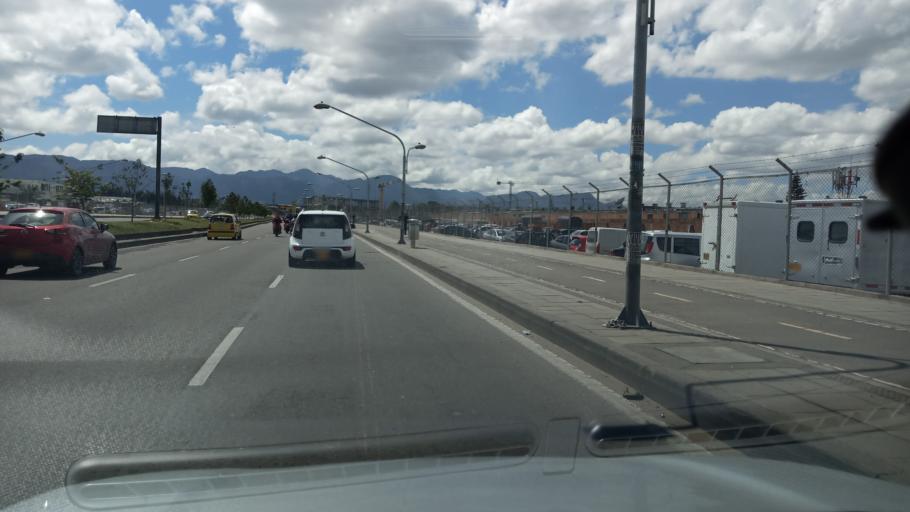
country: CO
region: Bogota D.C.
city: Bogota
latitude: 4.6881
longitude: -74.1181
